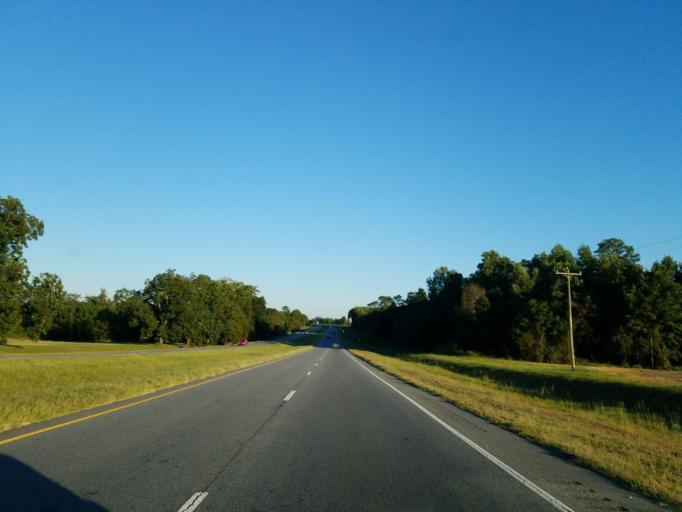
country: US
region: Georgia
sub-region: Worth County
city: Sylvester
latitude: 31.4872
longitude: -83.7018
